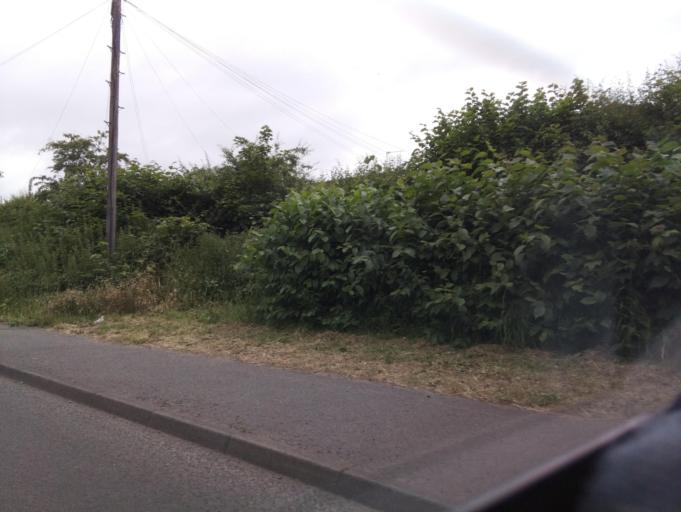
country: GB
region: England
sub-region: Staffordshire
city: Stafford
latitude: 52.7778
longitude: -2.1127
